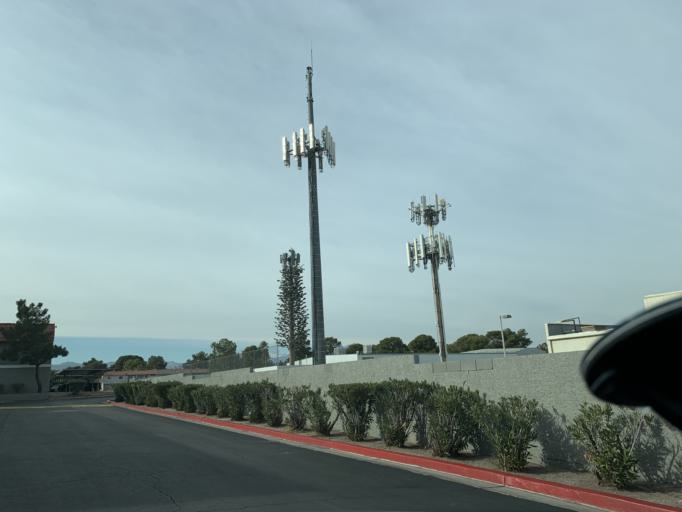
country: US
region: Nevada
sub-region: Clark County
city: Spring Valley
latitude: 36.0983
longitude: -115.2264
